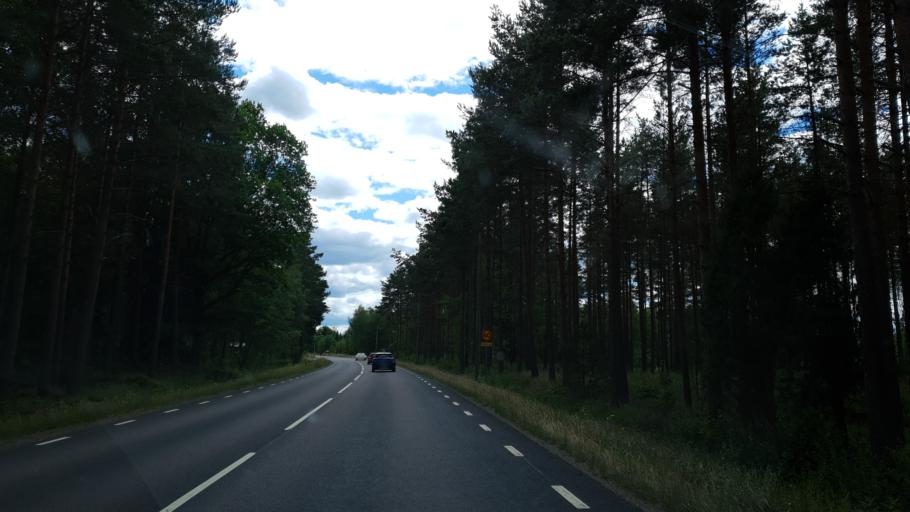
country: SE
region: Kalmar
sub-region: Emmaboda Kommun
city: Emmaboda
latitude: 56.9237
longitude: 15.5714
